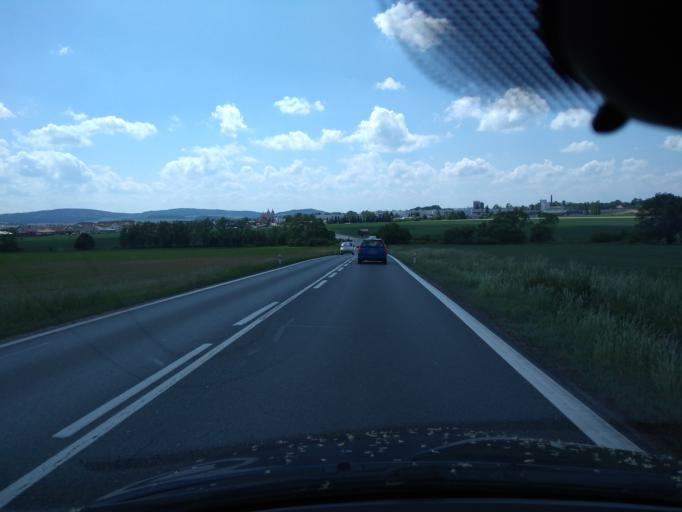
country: CZ
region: Plzensky
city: Prestice
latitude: 49.5885
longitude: 13.3267
